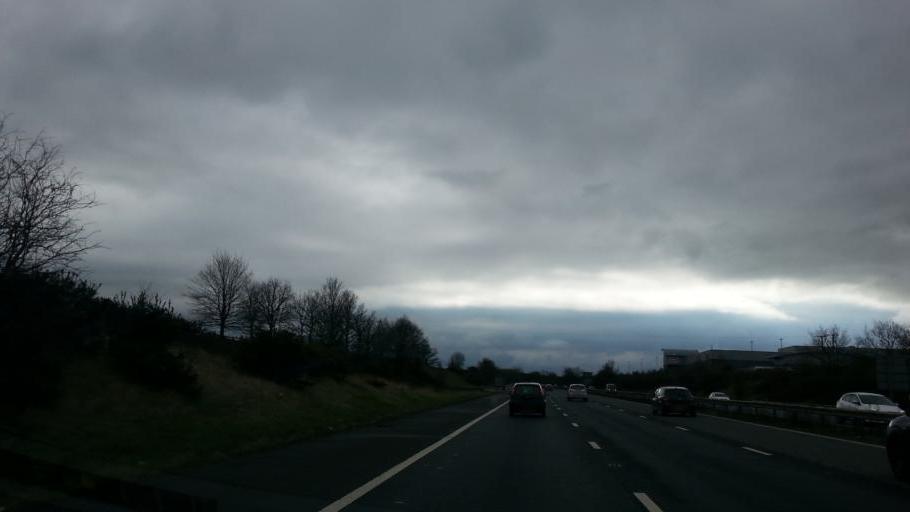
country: GB
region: England
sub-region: Somerset
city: North Petherton
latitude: 51.1009
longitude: -2.9950
